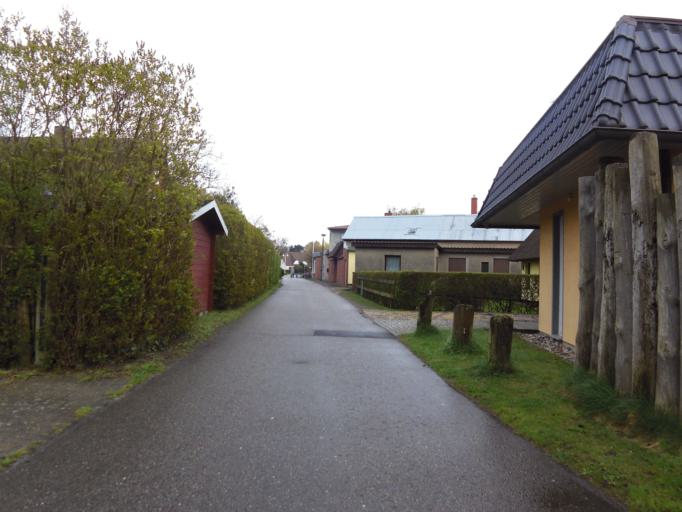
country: DE
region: Mecklenburg-Vorpommern
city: Zingst
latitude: 54.4337
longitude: 12.6875
